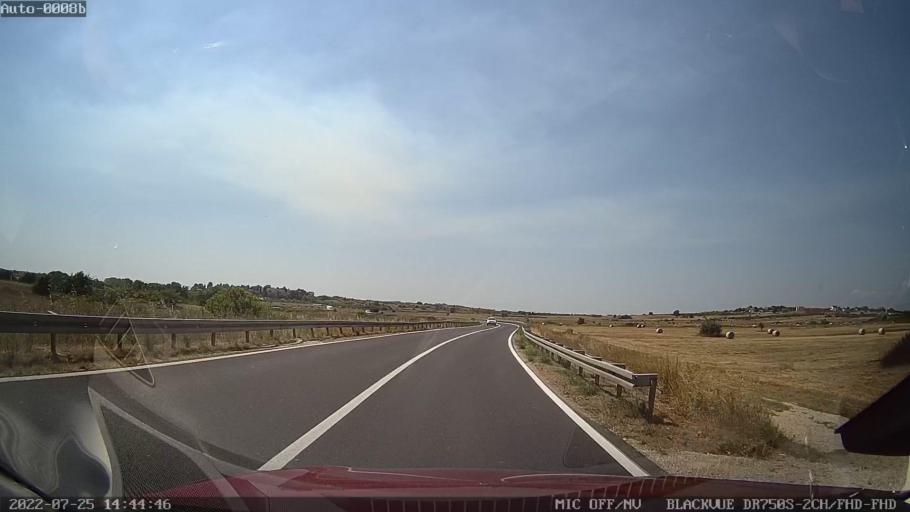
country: HR
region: Zadarska
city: Galovac
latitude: 44.1125
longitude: 15.3994
